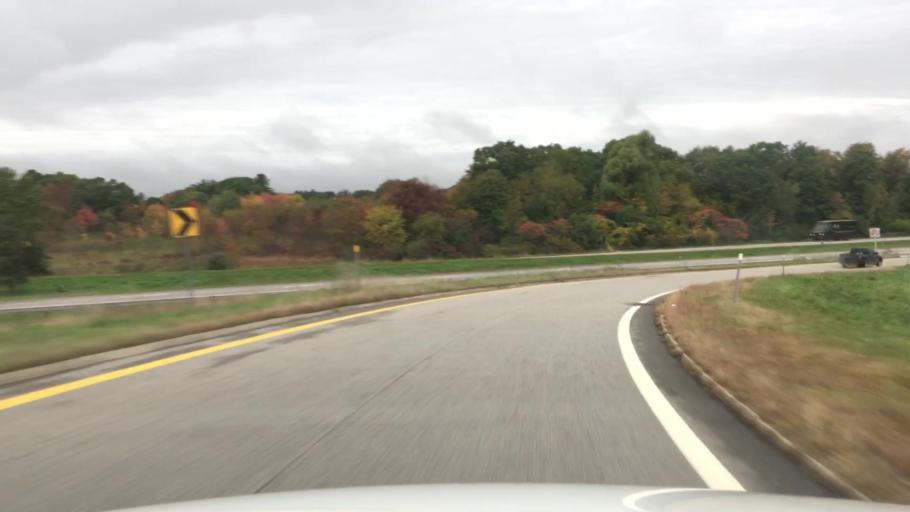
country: US
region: New Hampshire
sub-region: Rockingham County
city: Portsmouth
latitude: 43.0725
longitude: -70.7868
